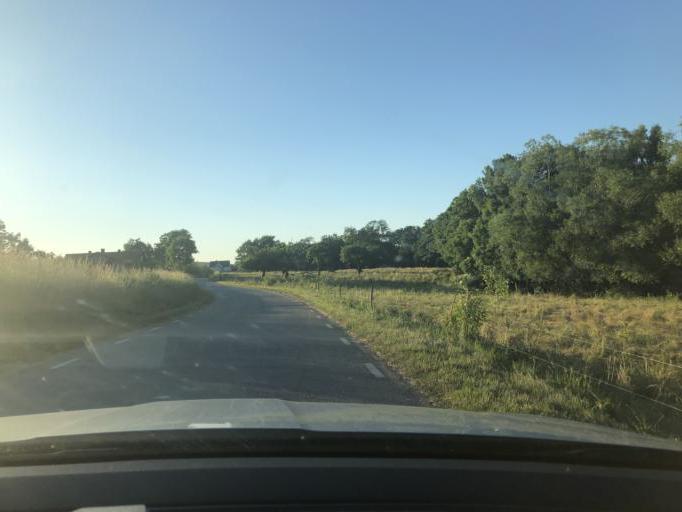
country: SE
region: Blekinge
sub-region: Karlshamns Kommun
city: Morrum
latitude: 56.1418
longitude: 14.6457
